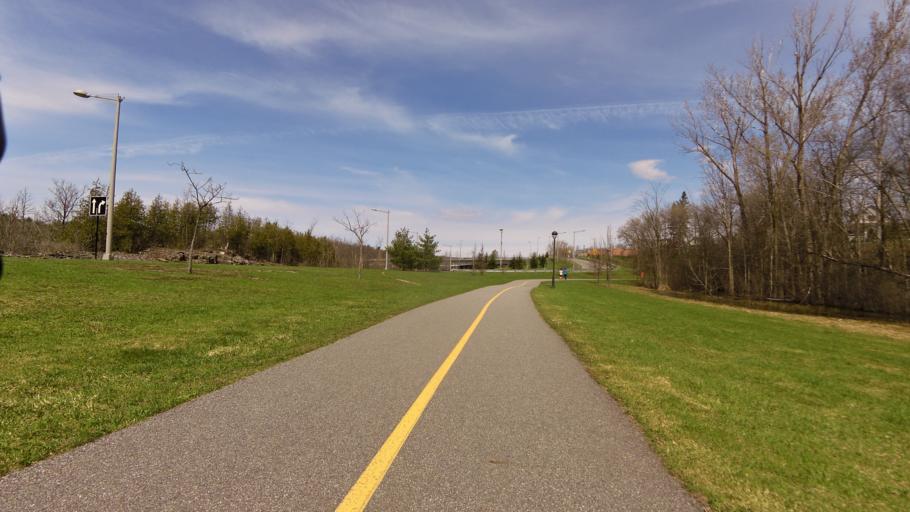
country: CA
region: Ontario
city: Ottawa
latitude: 45.4304
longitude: -75.7423
